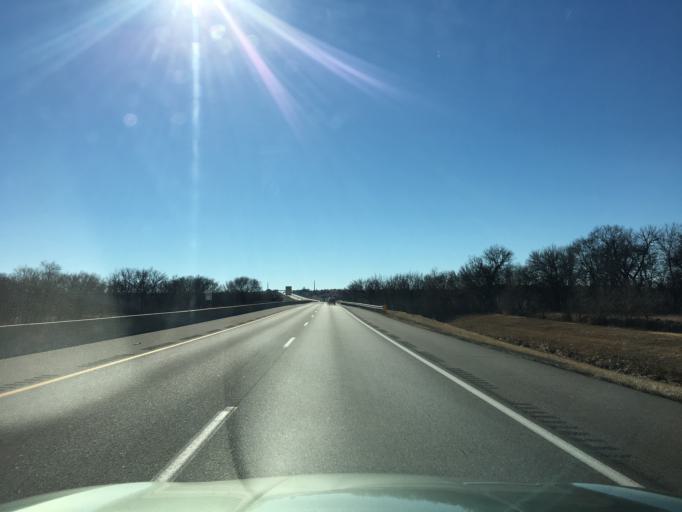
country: US
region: Kansas
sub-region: Sumner County
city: Wellington
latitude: 37.2184
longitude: -97.3391
